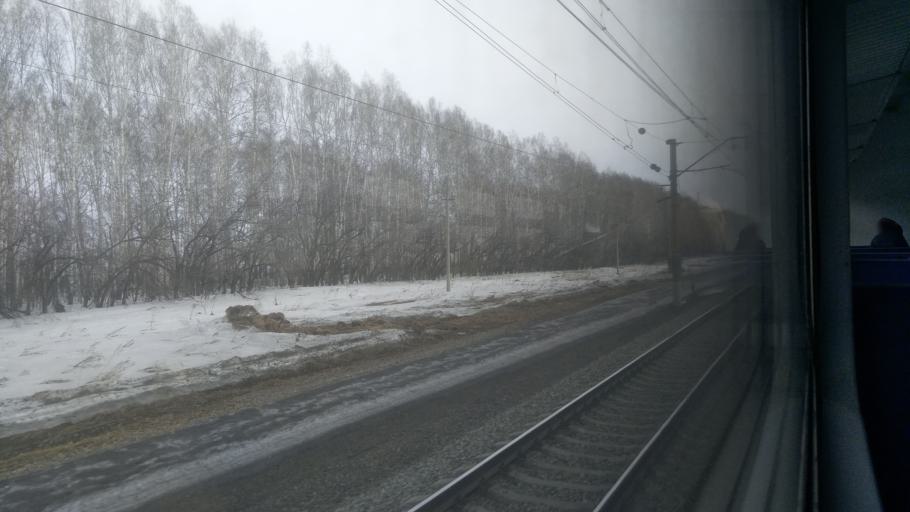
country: RU
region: Novosibirsk
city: Bolotnoye
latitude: 55.6971
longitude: 84.5530
